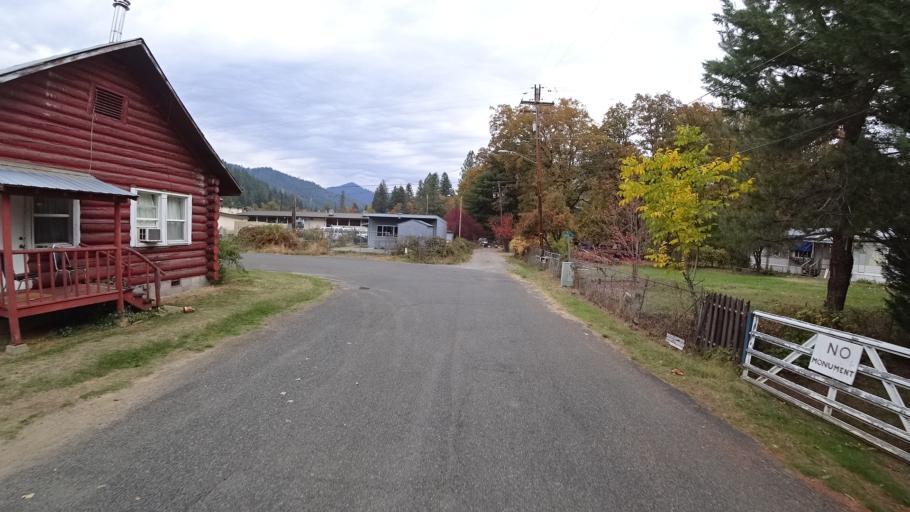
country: US
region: California
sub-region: Siskiyou County
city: Happy Camp
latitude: 41.7945
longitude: -123.3767
